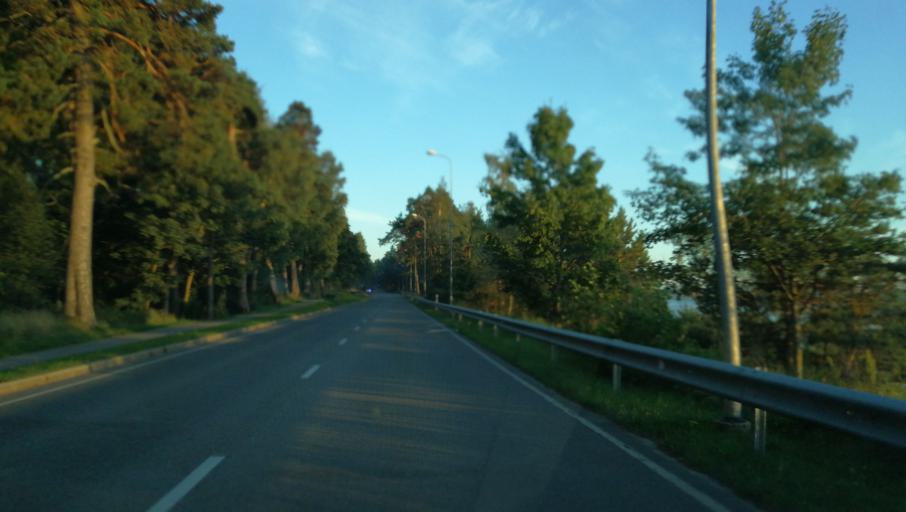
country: LV
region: Saulkrastu
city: Saulkrasti
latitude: 57.2879
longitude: 24.4127
